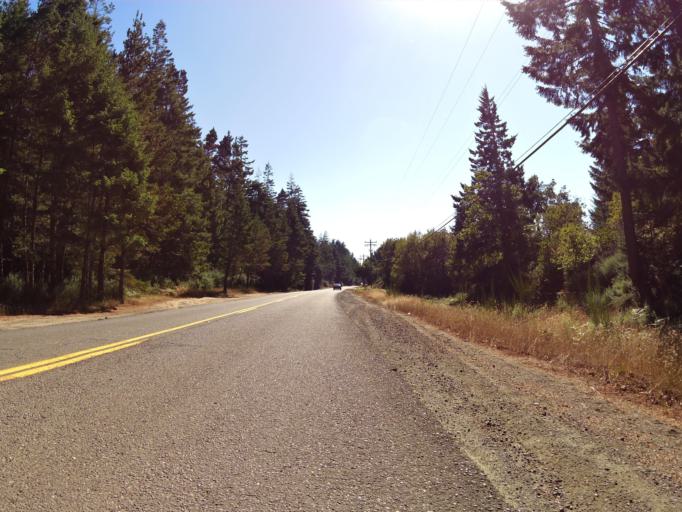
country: US
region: Oregon
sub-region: Coos County
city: Bandon
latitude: 43.1783
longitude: -124.3708
